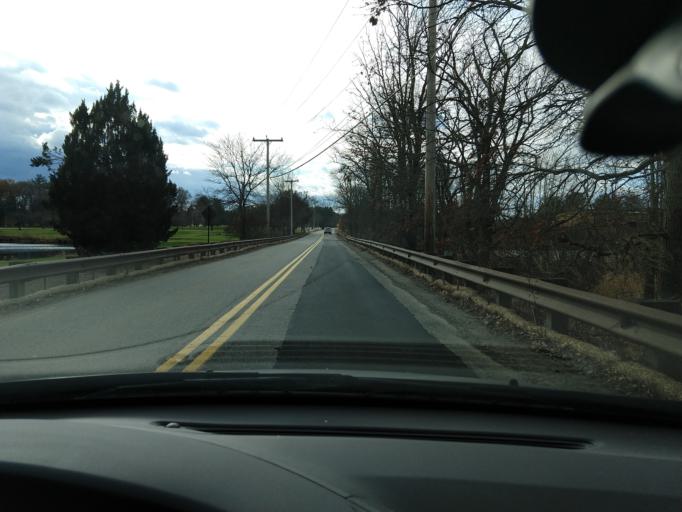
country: US
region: Massachusetts
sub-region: Middlesex County
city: West Concord
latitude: 42.4176
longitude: -71.3737
